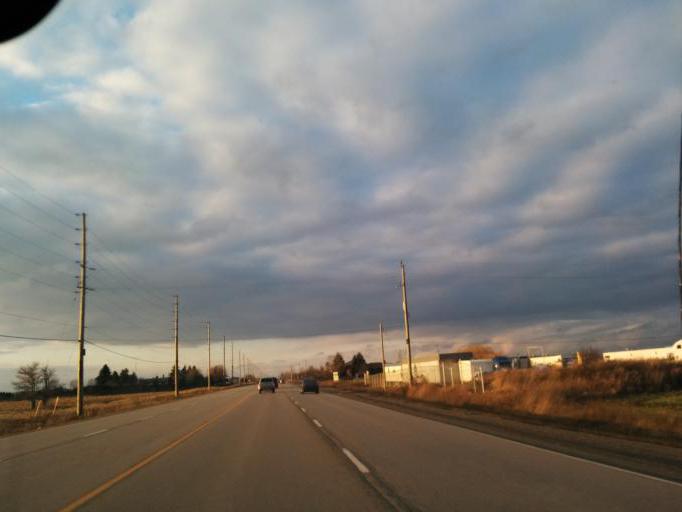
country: CA
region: Ontario
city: Brampton
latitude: 43.8413
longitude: -79.7090
